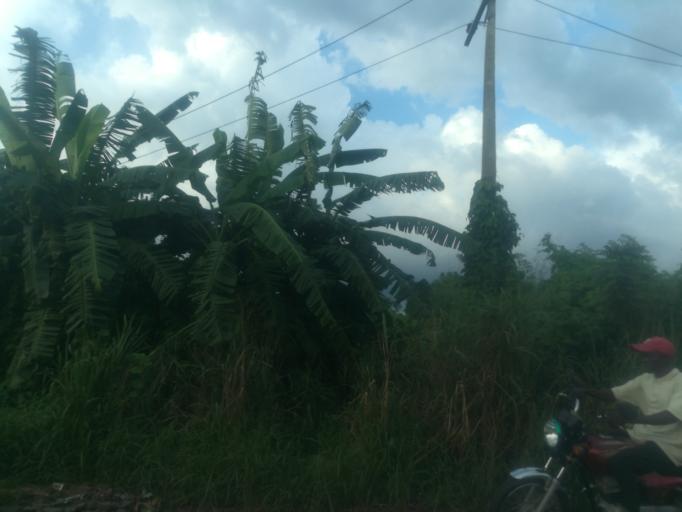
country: NG
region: Oyo
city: Ibadan
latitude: 7.3793
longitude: 3.8441
